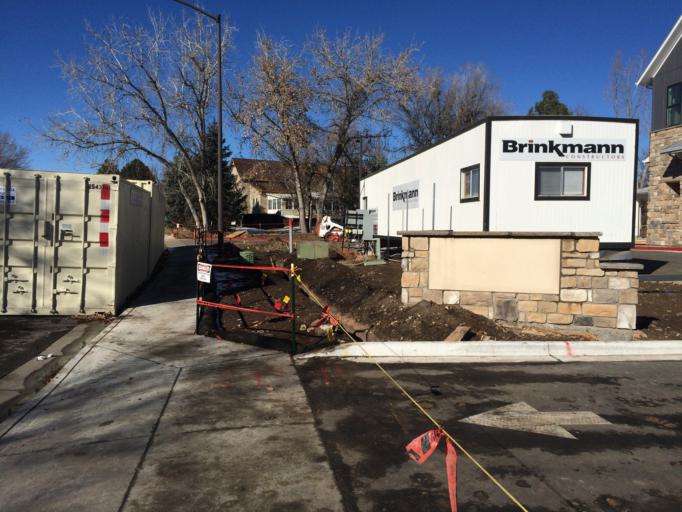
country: US
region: Colorado
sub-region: Boulder County
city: Louisville
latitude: 39.9896
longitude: -105.1233
